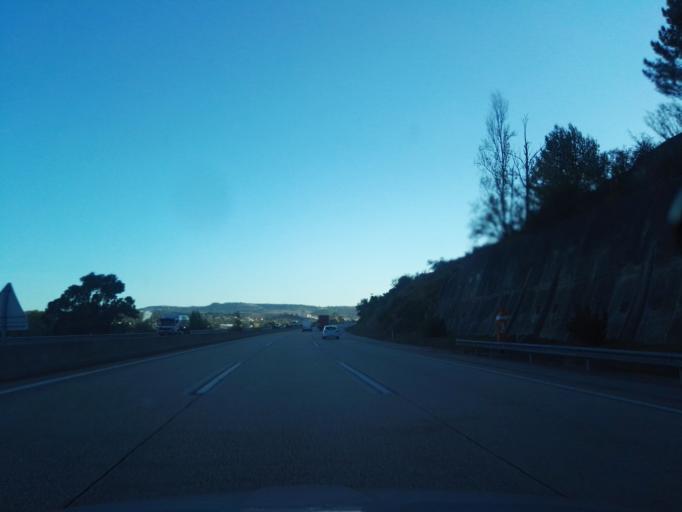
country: PT
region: Lisbon
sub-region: Loures
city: Bucelas
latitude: 38.8931
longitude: -9.1228
